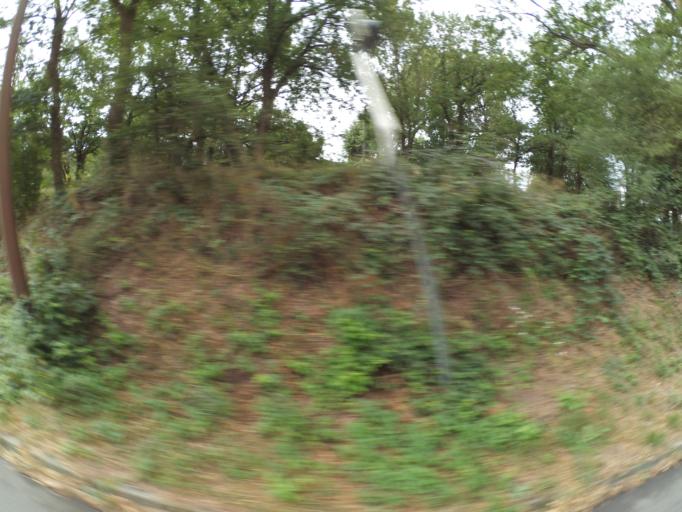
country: FR
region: Pays de la Loire
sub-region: Departement de Maine-et-Loire
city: Montfaucon-Montigne
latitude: 47.0913
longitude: -1.1315
